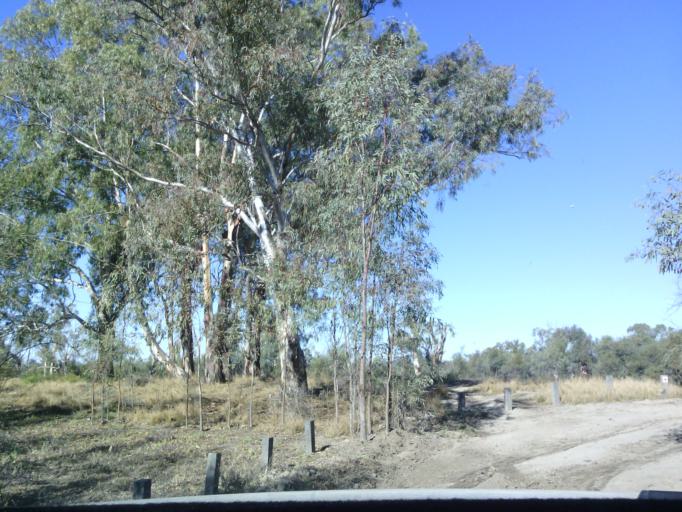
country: AU
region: South Australia
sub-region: Berri and Barmera
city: Berri
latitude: -34.2605
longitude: 140.6903
